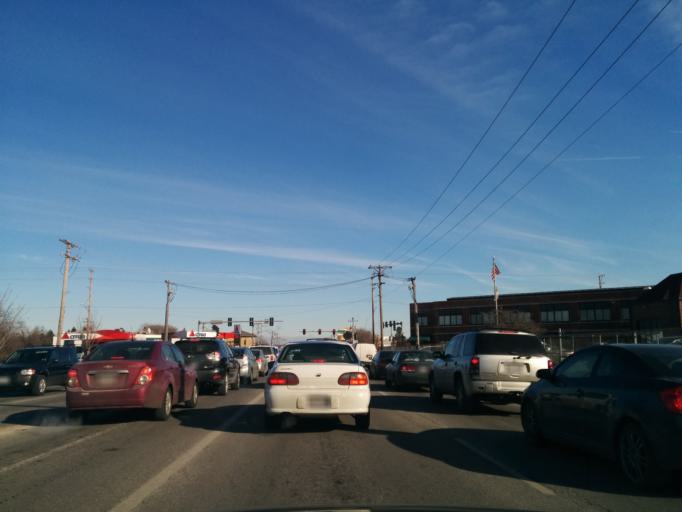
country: US
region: Illinois
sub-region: Cook County
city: Northlake
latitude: 41.9303
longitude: -87.8861
